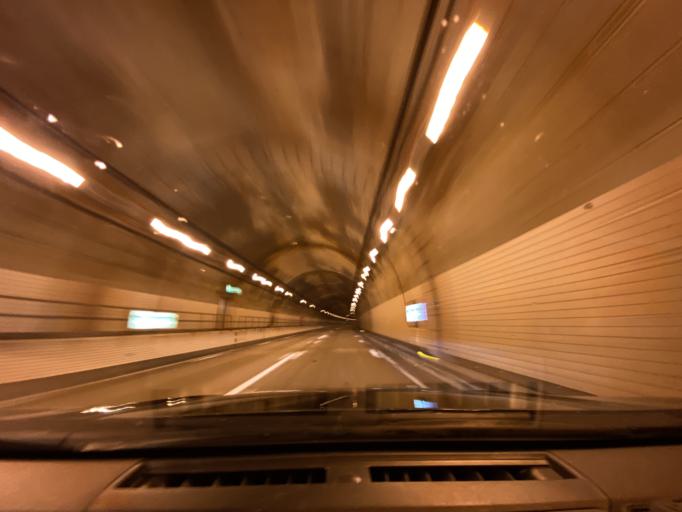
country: JP
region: Hokkaido
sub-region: Asahikawa-shi
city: Asahikawa
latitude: 43.7838
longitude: 142.2335
